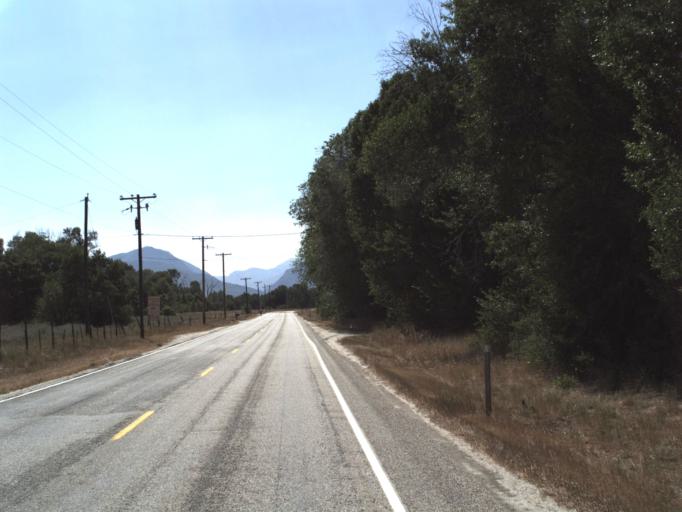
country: US
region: Utah
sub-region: Weber County
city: Wolf Creek
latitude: 41.2610
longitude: -111.7115
